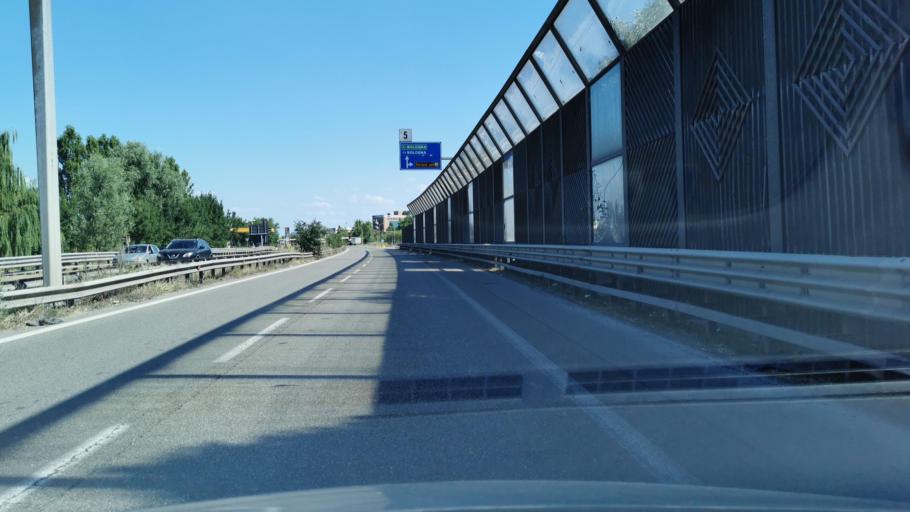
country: IT
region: Emilia-Romagna
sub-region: Provincia di Modena
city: Modena
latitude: 44.6557
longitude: 10.9553
